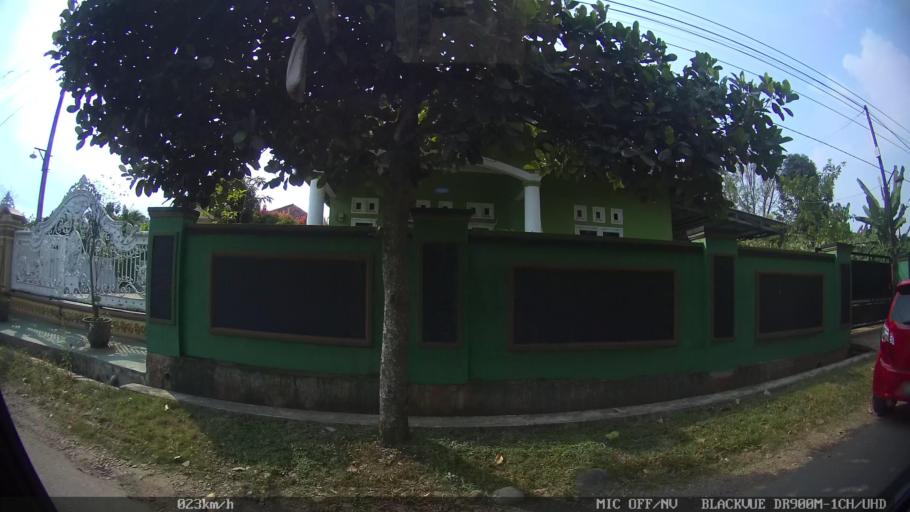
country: ID
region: Lampung
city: Kedaton
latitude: -5.3524
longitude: 105.2253
